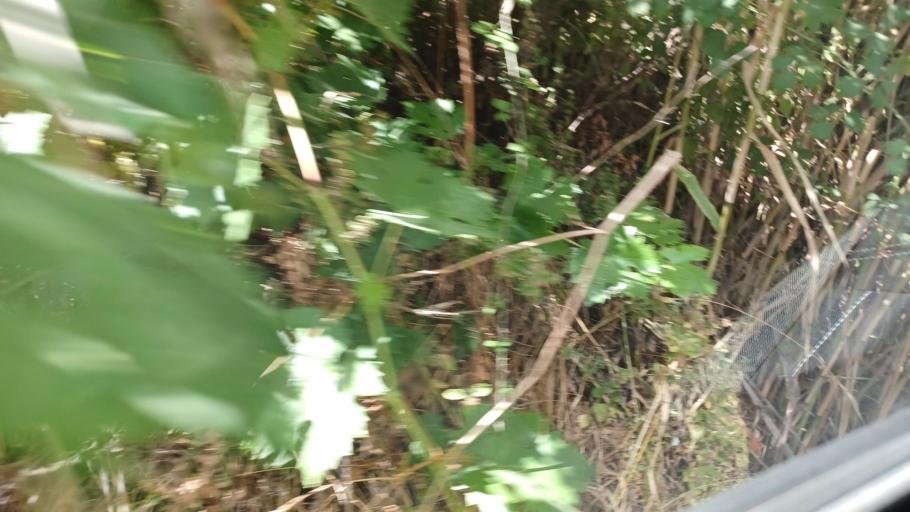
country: CY
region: Pafos
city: Mesogi
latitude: 34.8791
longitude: 32.5080
